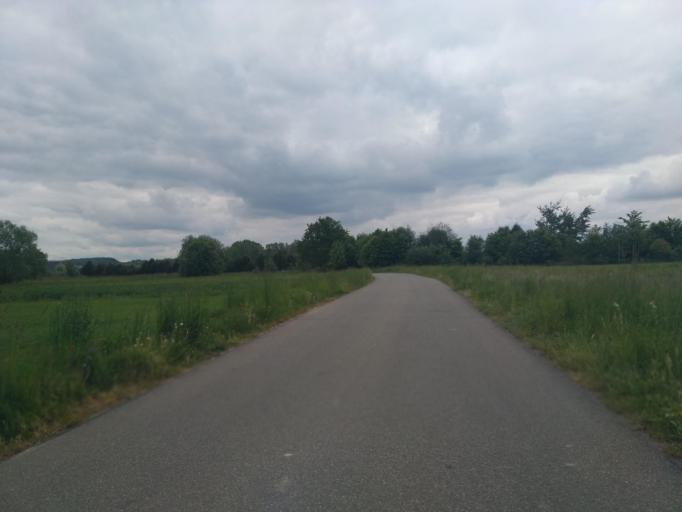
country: PL
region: Subcarpathian Voivodeship
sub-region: Powiat krosnienski
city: Jedlicze
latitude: 49.7065
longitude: 21.6771
